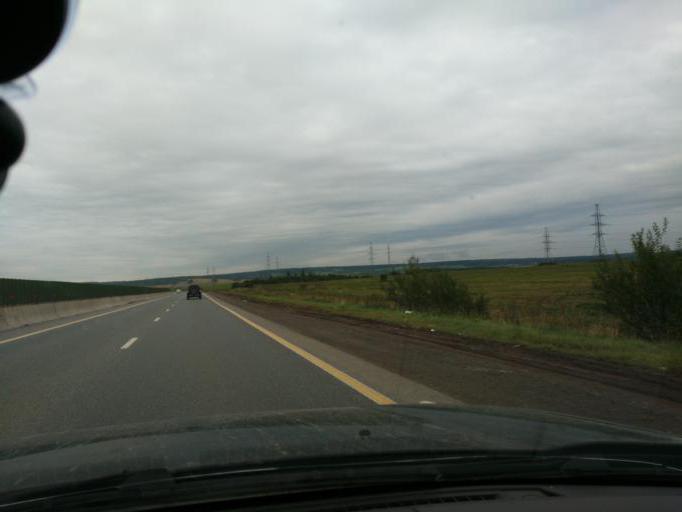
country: RU
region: Perm
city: Ferma
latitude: 57.9303
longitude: 56.3087
